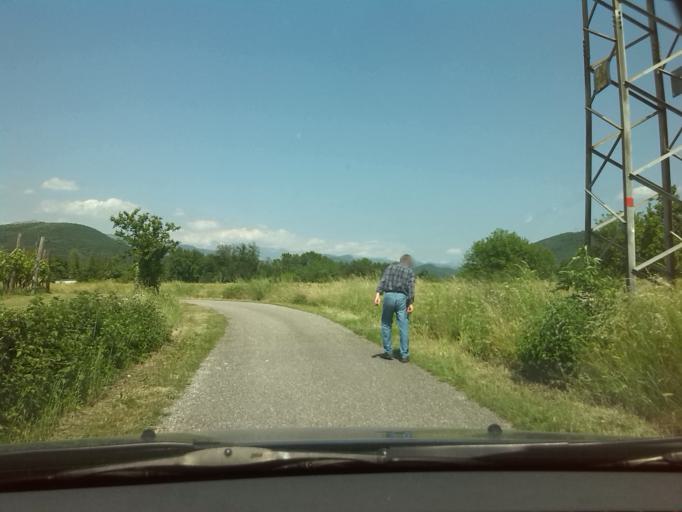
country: IT
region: Friuli Venezia Giulia
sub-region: Provincia di Udine
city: Cividale del Friuli
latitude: 46.0955
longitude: 13.4433
